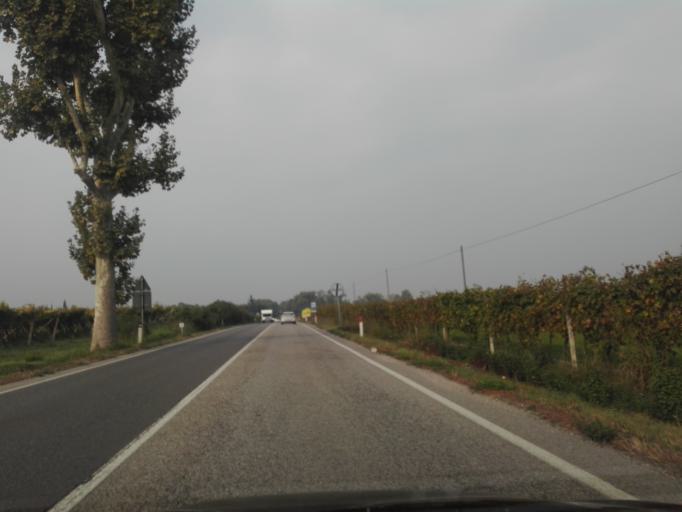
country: IT
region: Veneto
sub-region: Provincia di Verona
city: San Giorgio in Salici
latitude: 45.4400
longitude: 10.7791
